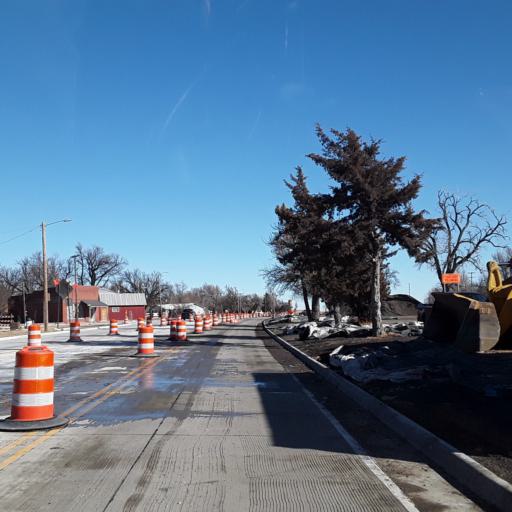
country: US
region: Kansas
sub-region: Pawnee County
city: Larned
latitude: 38.0749
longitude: -99.2437
